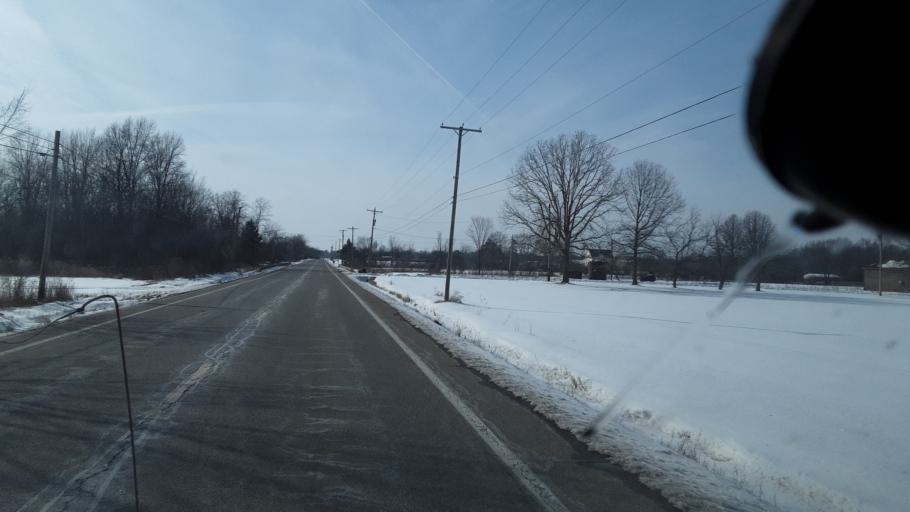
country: US
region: Ohio
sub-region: Mahoning County
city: Craig Beach
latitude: 41.0245
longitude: -80.9653
